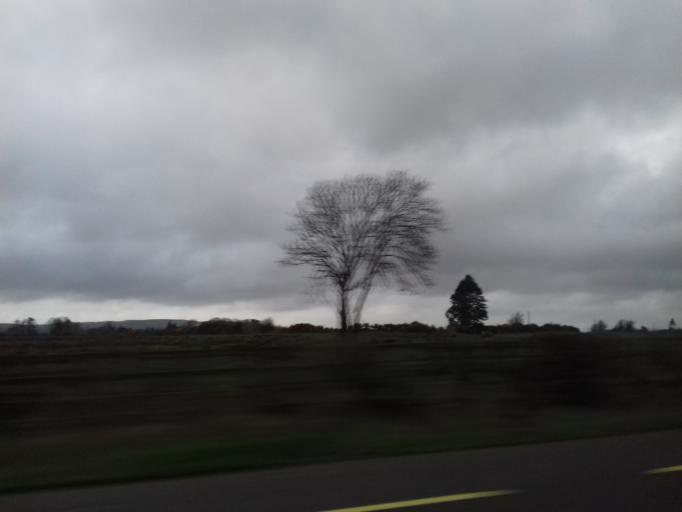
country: IE
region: Munster
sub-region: County Limerick
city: Abbeyfeale
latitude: 52.3575
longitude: -9.3253
